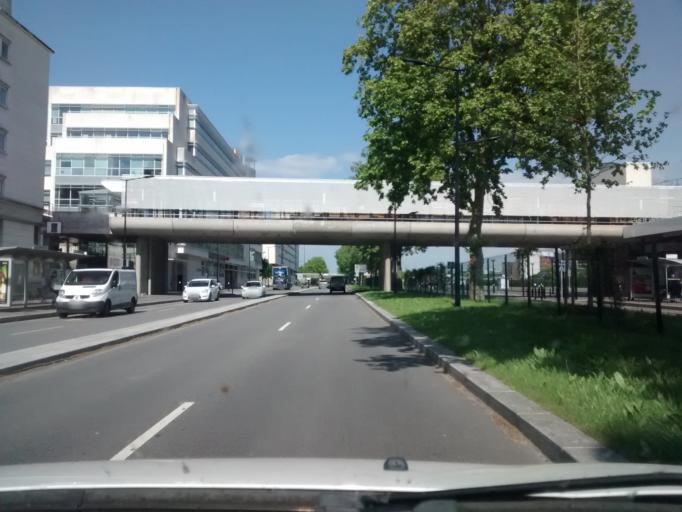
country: FR
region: Ile-de-France
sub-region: Departement des Yvelines
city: Bois-d'Arcy
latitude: 48.7878
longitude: 2.0434
